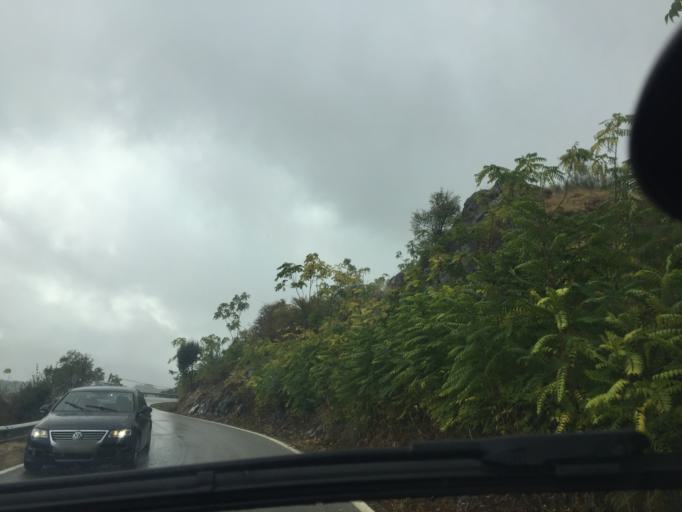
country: ES
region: Andalusia
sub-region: Provincia de Jaen
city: Jimena
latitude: 37.8234
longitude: -3.4635
